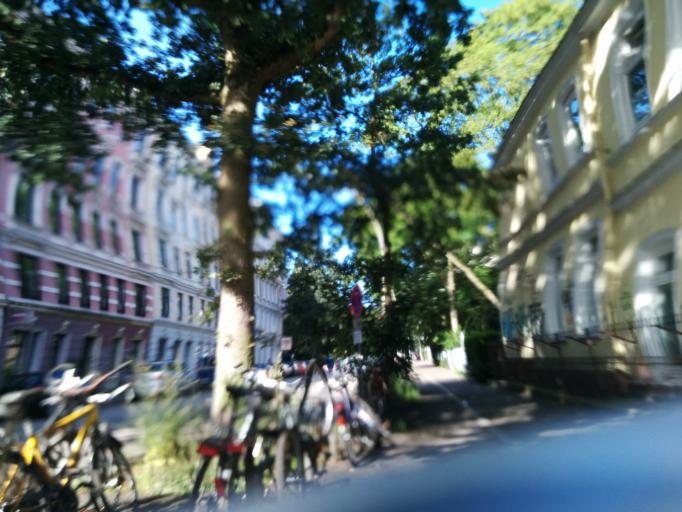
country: DE
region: Hamburg
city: Altona
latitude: 53.5509
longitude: 9.9247
